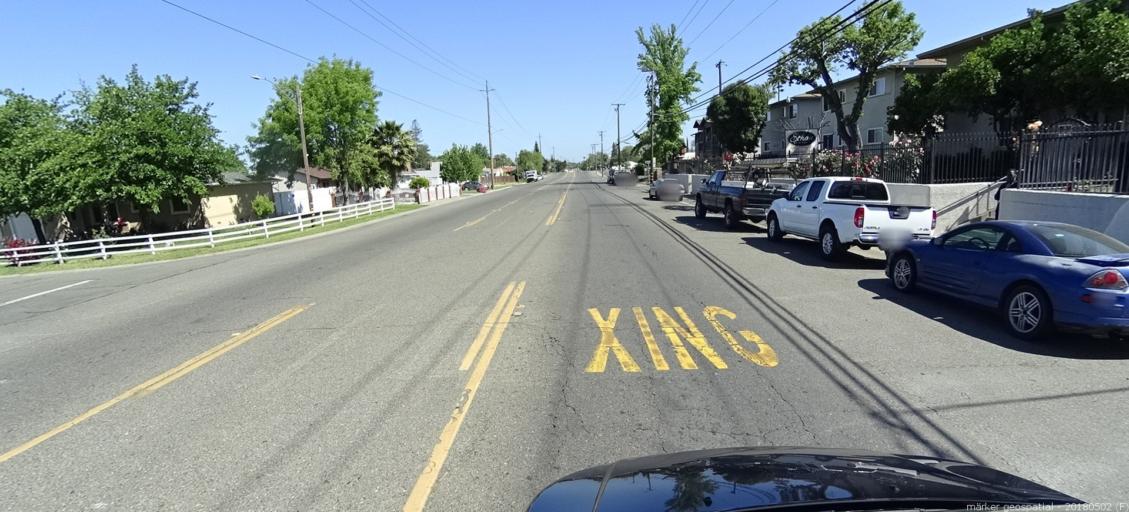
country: US
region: California
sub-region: Sacramento County
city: Arden-Arcade
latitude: 38.6009
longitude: -121.4200
